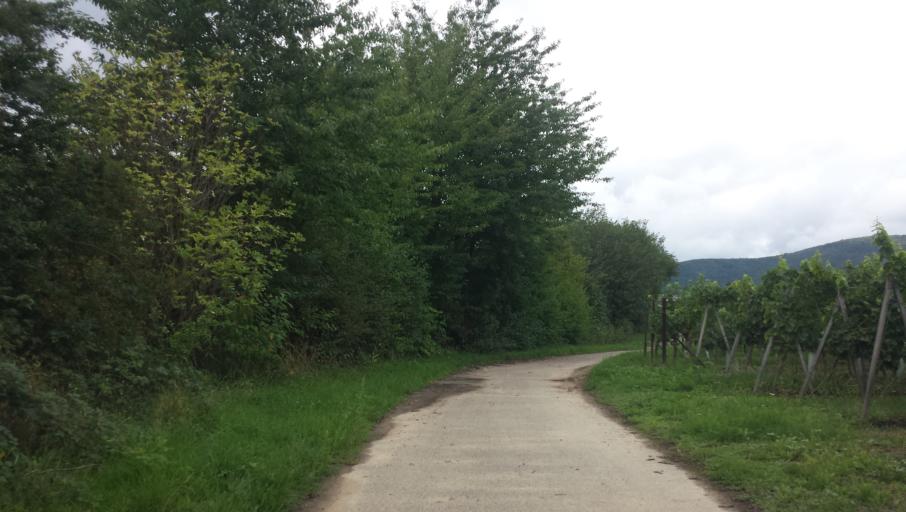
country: DE
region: Rheinland-Pfalz
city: Bochingen
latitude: 49.2370
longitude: 8.0989
